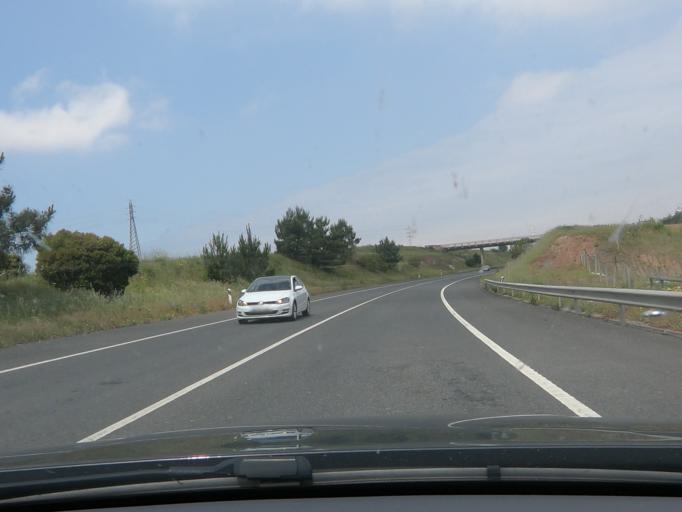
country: PT
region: Leiria
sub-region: Peniche
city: Atouguia da Baleia
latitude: 39.3237
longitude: -9.3100
